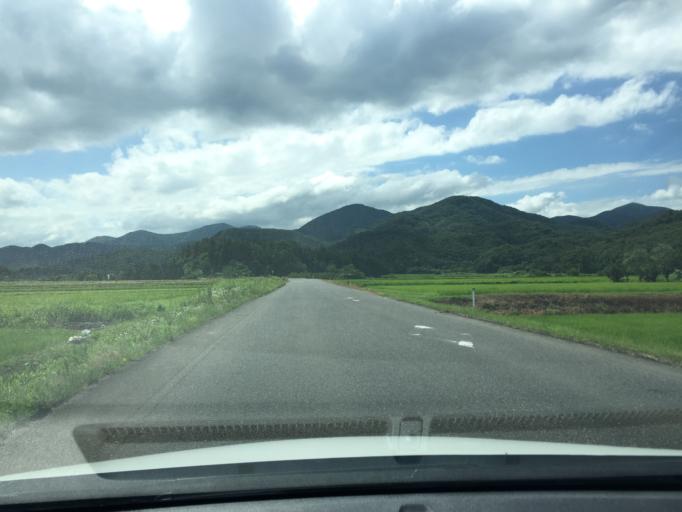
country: JP
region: Fukushima
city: Koriyama
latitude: 37.3454
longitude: 140.2597
